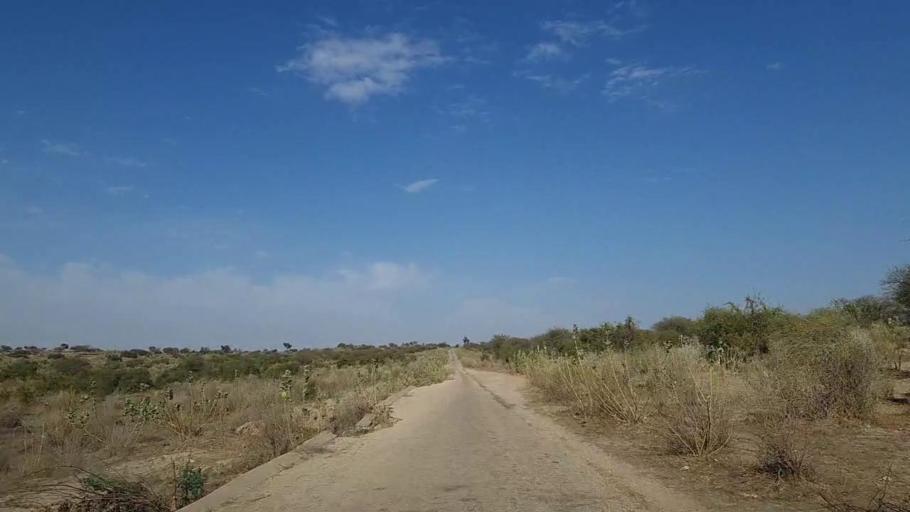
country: PK
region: Sindh
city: Naukot
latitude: 24.8450
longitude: 69.5546
